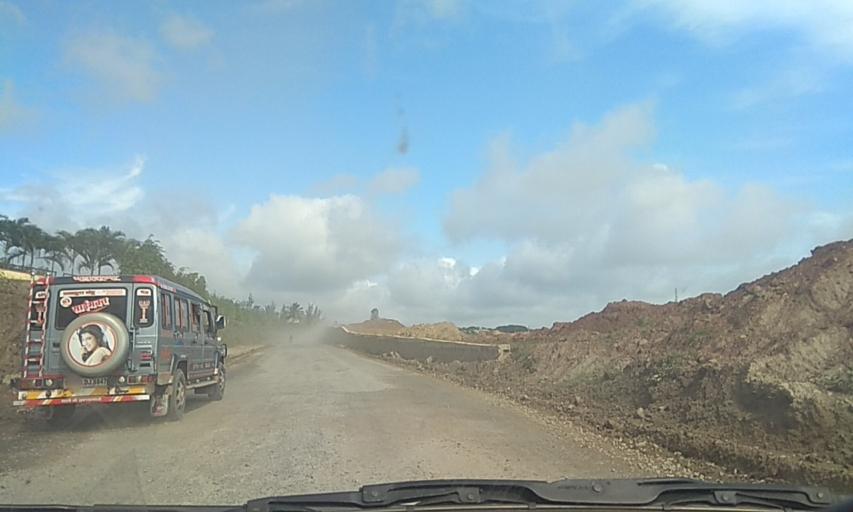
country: IN
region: Karnataka
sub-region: Haveri
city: Shiggaon
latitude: 15.0345
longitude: 75.1767
